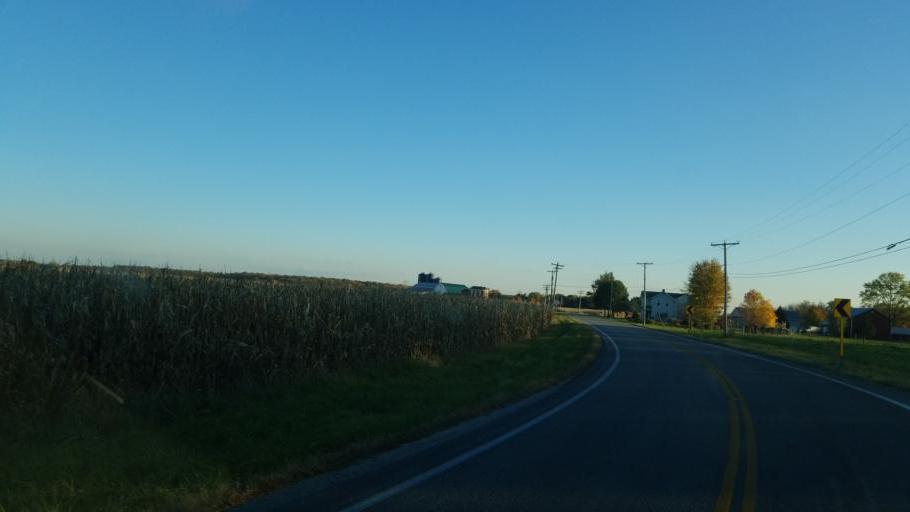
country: US
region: Ohio
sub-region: Sandusky County
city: Green Springs
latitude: 41.3151
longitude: -83.0581
